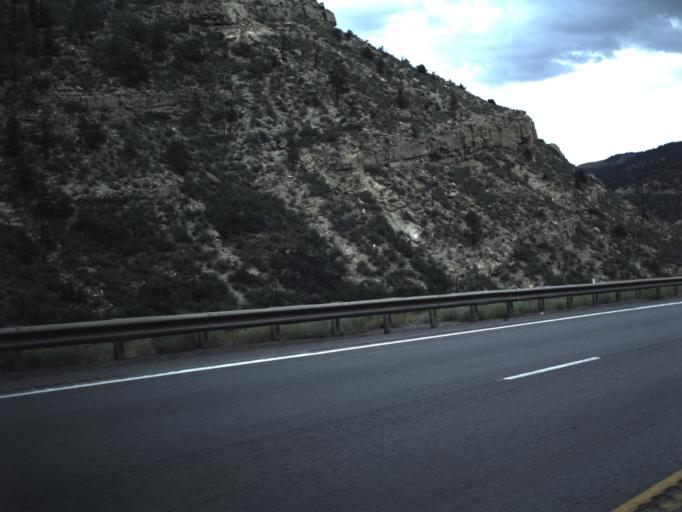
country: US
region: Utah
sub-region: Carbon County
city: Helper
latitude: 39.7943
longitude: -110.9319
